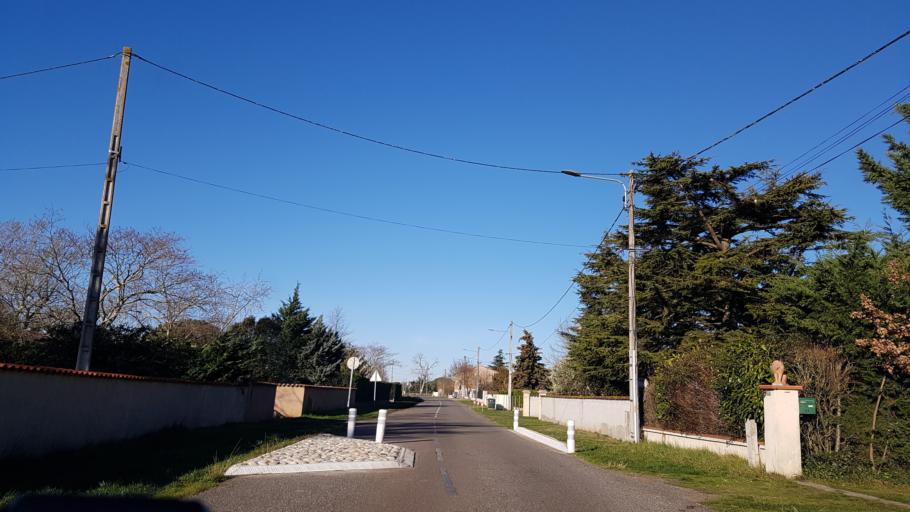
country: FR
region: Midi-Pyrenees
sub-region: Departement de la Haute-Garonne
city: Calmont
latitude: 43.2876
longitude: 1.6201
